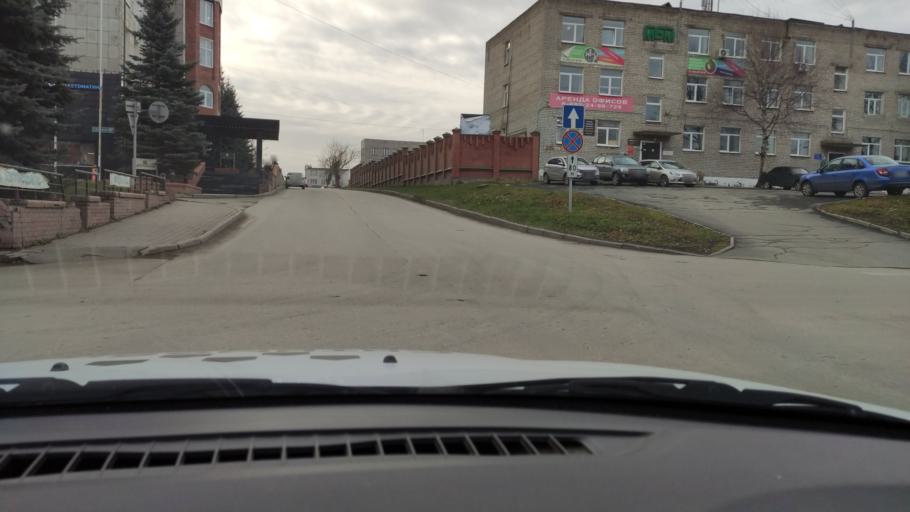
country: RU
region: Perm
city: Kondratovo
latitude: 57.9719
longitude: 56.1762
